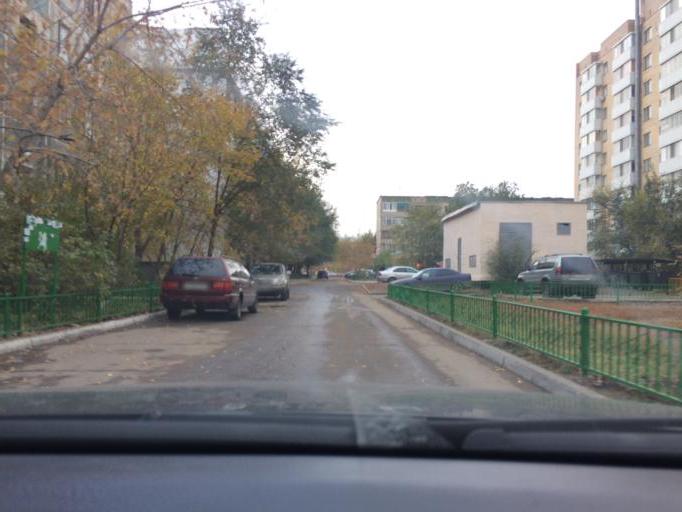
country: KZ
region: Astana Qalasy
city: Astana
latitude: 51.1476
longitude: 71.4665
